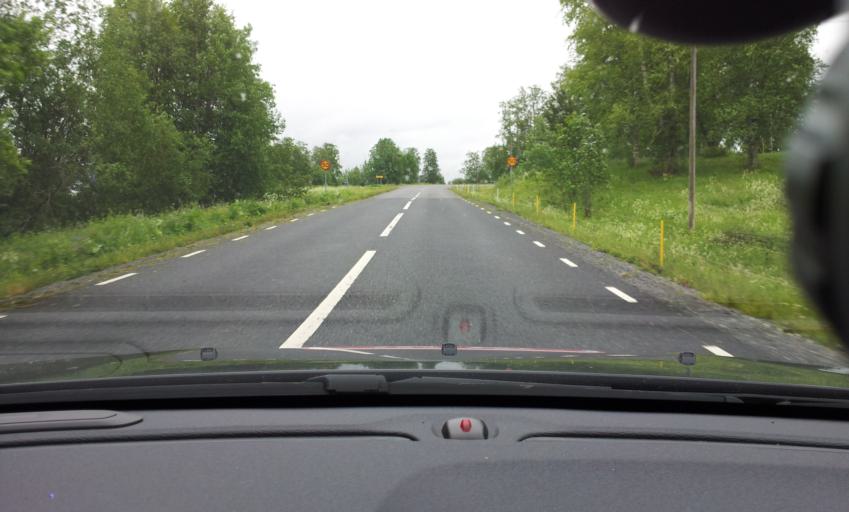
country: SE
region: Jaemtland
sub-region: Stroemsunds Kommun
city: Stroemsund
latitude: 63.6295
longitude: 15.2279
